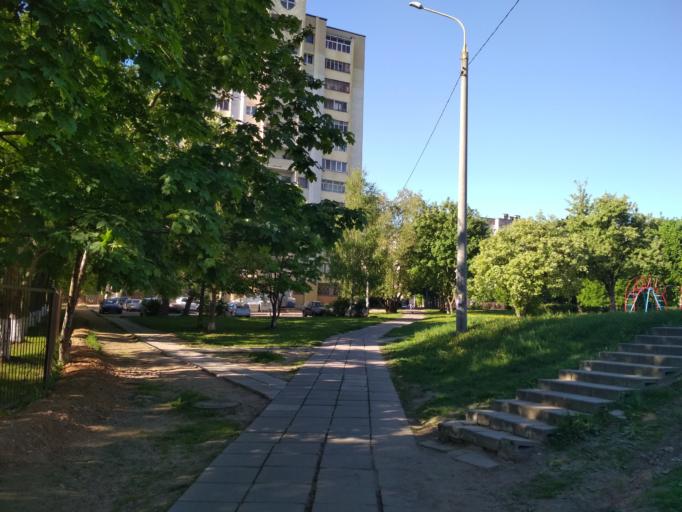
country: BY
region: Minsk
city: Minsk
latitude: 53.8812
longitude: 27.5453
